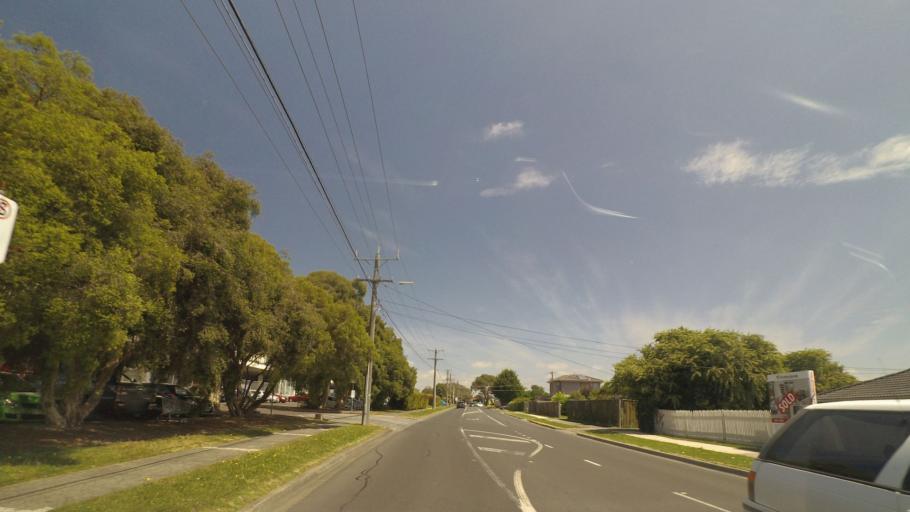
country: AU
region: Victoria
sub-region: Yarra Ranges
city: Chirnside Park
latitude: -37.7558
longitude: 145.3115
